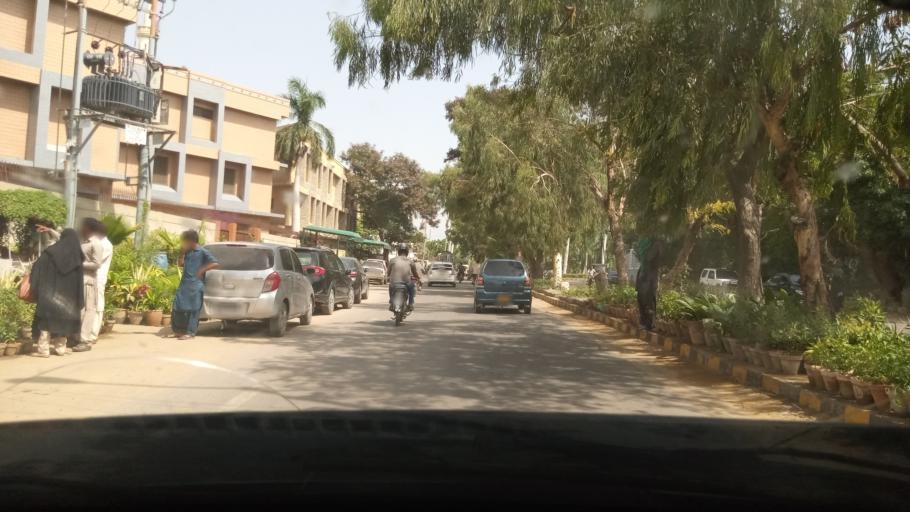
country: PK
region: Sindh
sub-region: Karachi District
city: Karachi
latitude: 24.8784
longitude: 67.0430
